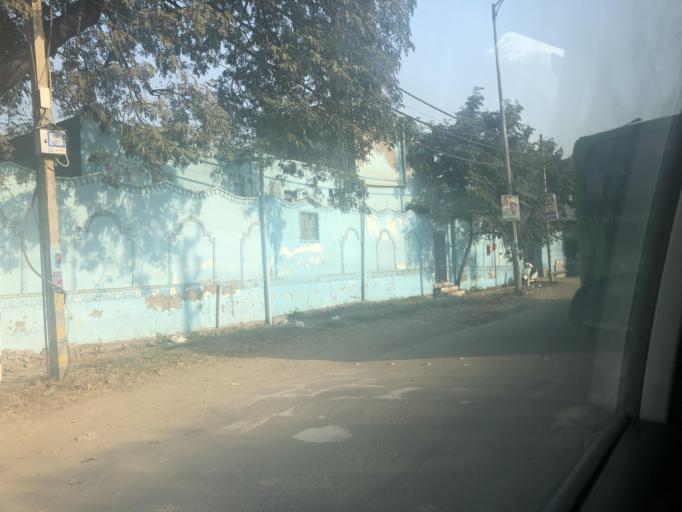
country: IN
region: Haryana
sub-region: Gurgaon
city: Gurgaon
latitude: 28.5578
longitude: 77.0045
